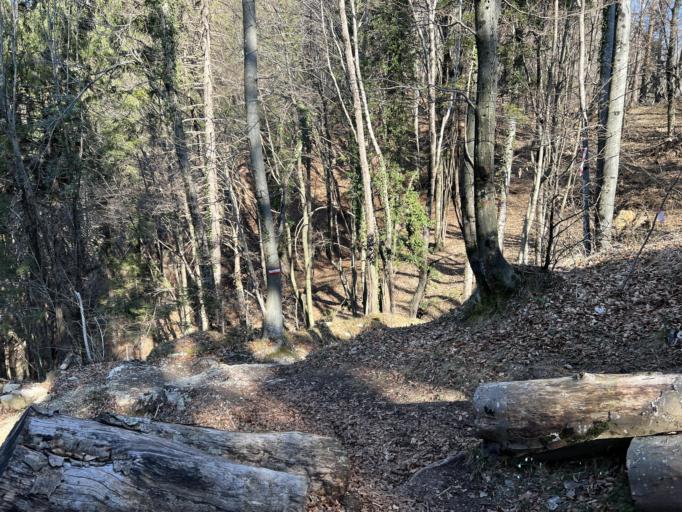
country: IT
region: Friuli Venezia Giulia
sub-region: Provincia di Udine
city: Zuglio
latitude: 46.4365
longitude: 13.0462
